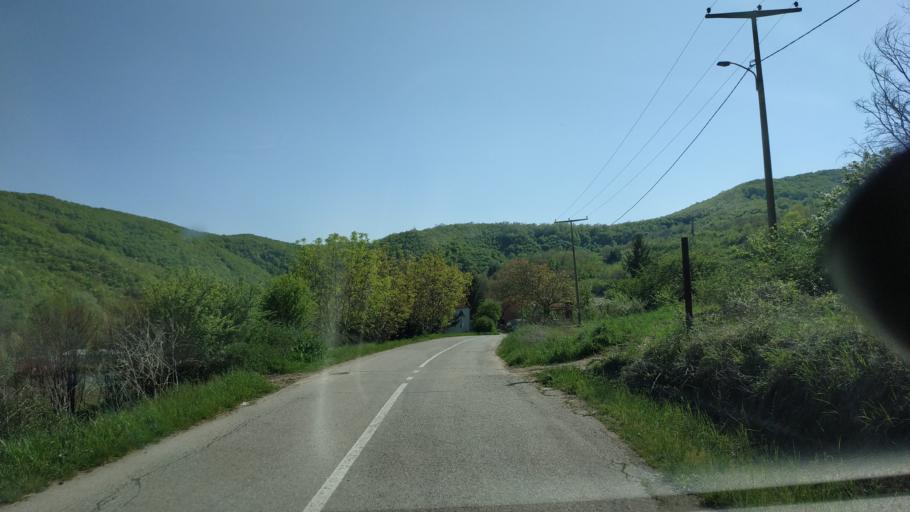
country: RS
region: Central Serbia
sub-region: Nisavski Okrug
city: Nis
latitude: 43.4281
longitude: 21.8507
